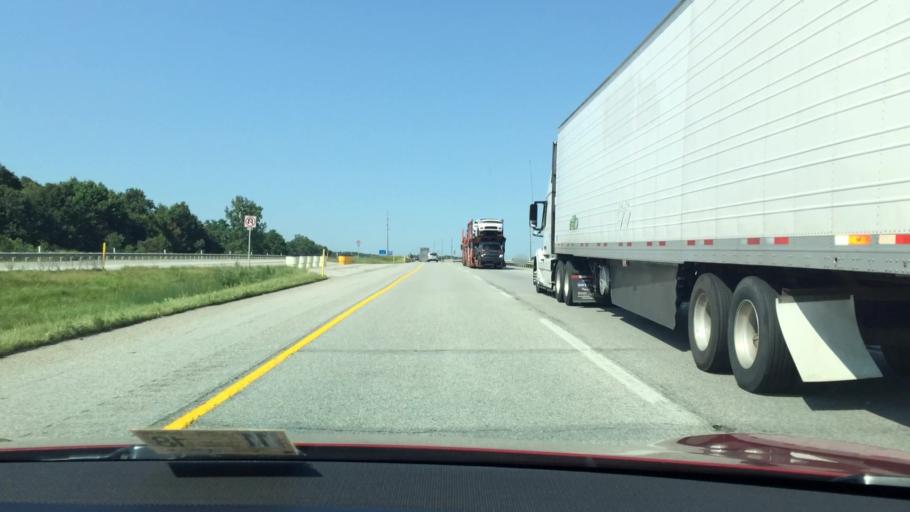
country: US
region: Indiana
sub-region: Elkhart County
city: Middlebury
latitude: 41.7433
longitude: -85.7249
